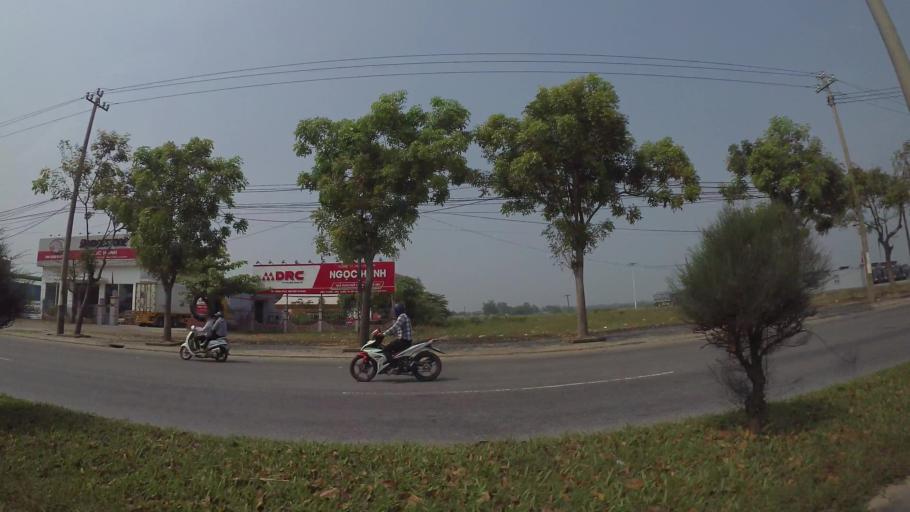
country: VN
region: Da Nang
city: Cam Le
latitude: 15.9695
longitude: 108.2097
